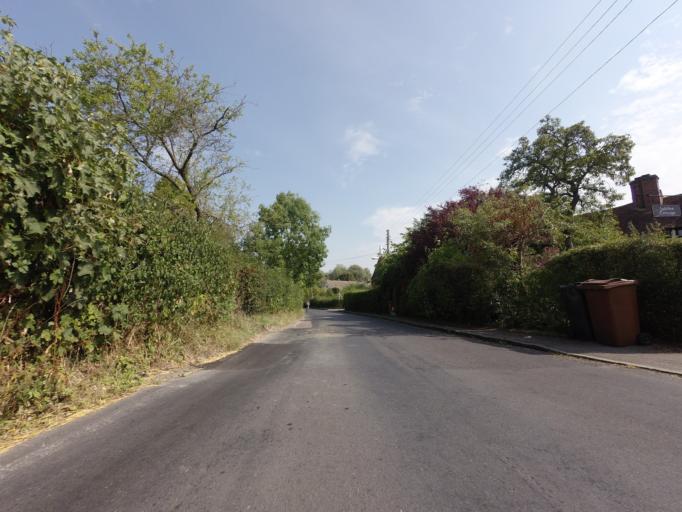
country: GB
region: England
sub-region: Kent
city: Headcorn
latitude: 51.1419
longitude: 0.5939
